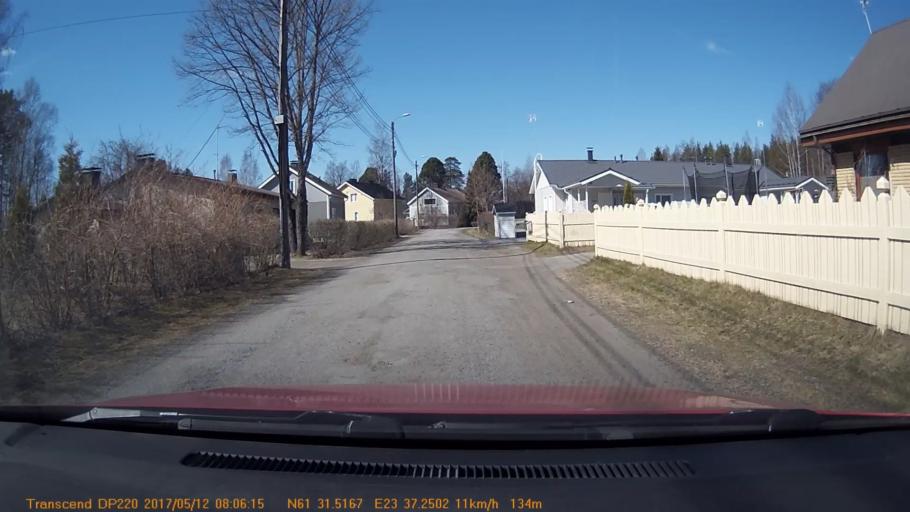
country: FI
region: Pirkanmaa
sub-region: Tampere
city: Yloejaervi
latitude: 61.5253
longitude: 23.6209
